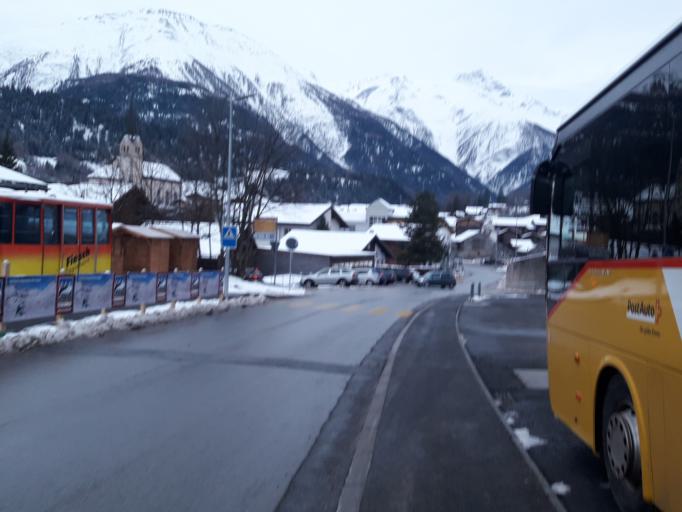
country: CH
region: Valais
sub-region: Goms District
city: Fiesch
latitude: 46.4064
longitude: 8.1347
